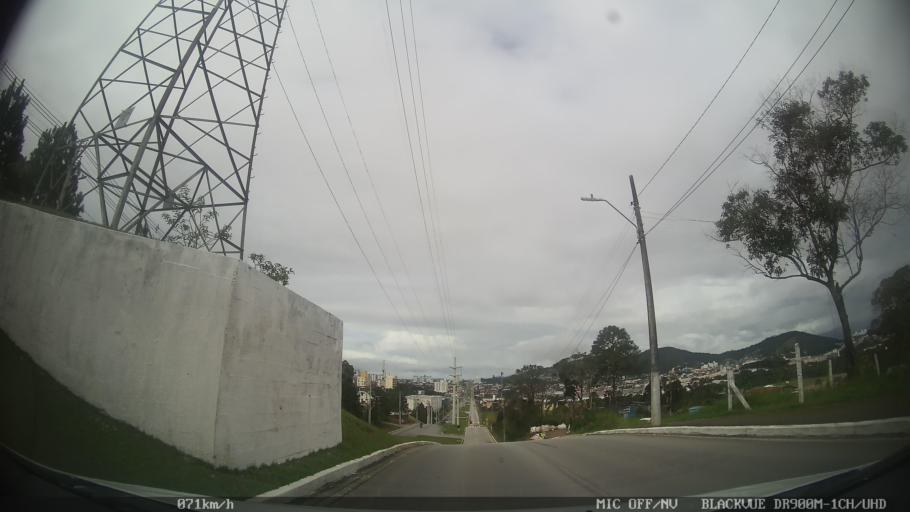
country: BR
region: Santa Catarina
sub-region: Sao Jose
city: Campinas
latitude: -27.5554
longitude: -48.6425
